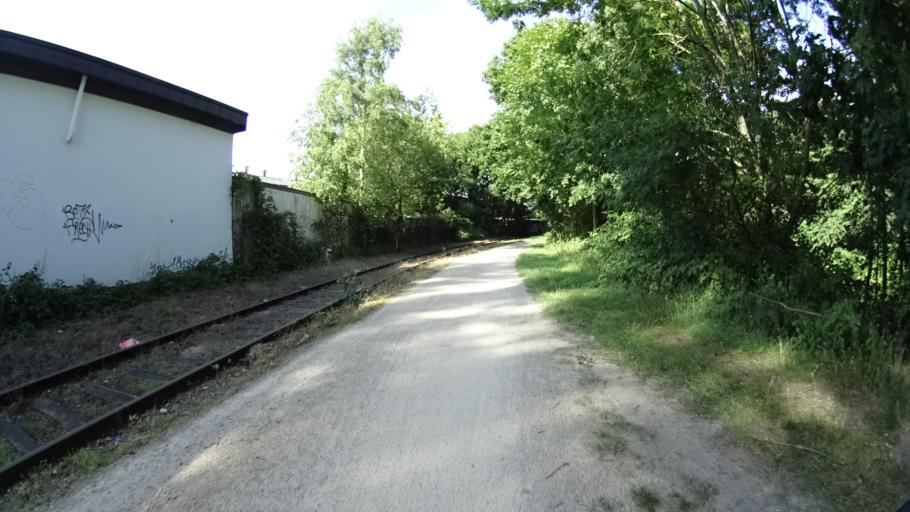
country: DE
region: Lower Saxony
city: Lueneburg
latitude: 53.2596
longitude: 10.4150
